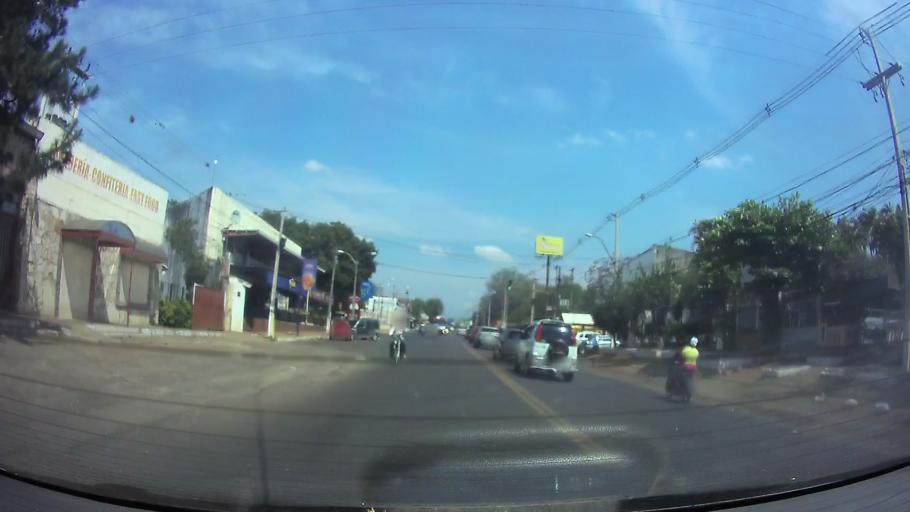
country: PY
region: Central
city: San Lorenzo
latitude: -25.3644
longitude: -57.4827
